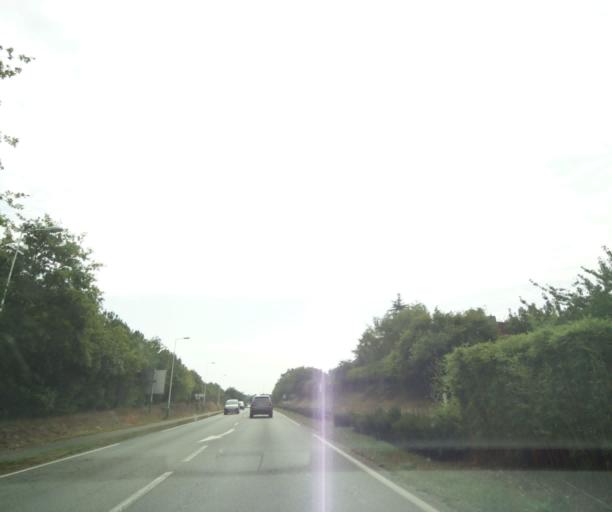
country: FR
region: Pays de la Loire
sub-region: Departement de la Loire-Atlantique
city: Saint-Herblain
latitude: 47.2140
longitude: -1.6366
